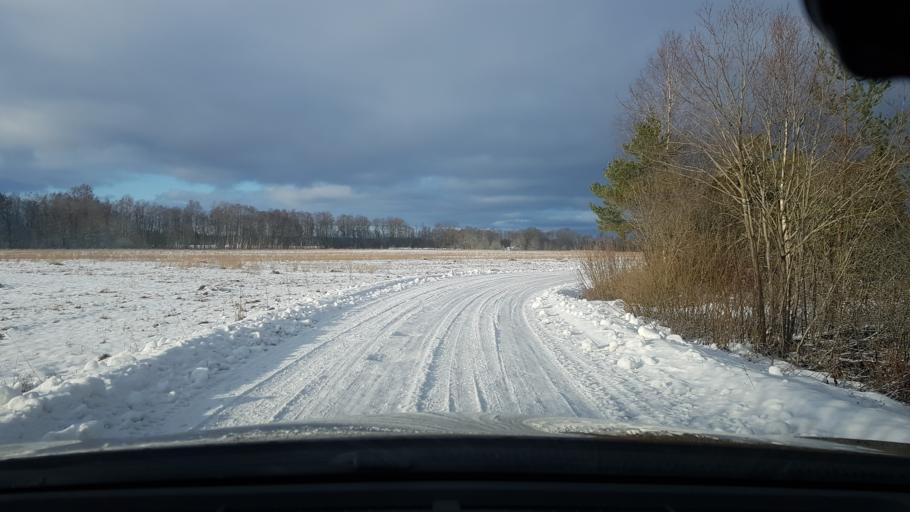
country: EE
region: Harju
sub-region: Keila linn
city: Keila
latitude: 59.2971
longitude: 24.2479
